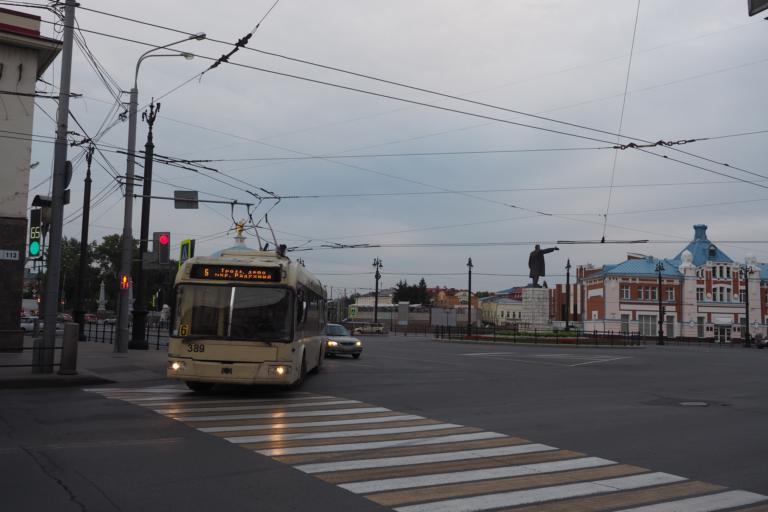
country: RU
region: Tomsk
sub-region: Tomskiy Rayon
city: Tomsk
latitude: 56.4886
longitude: 84.9479
